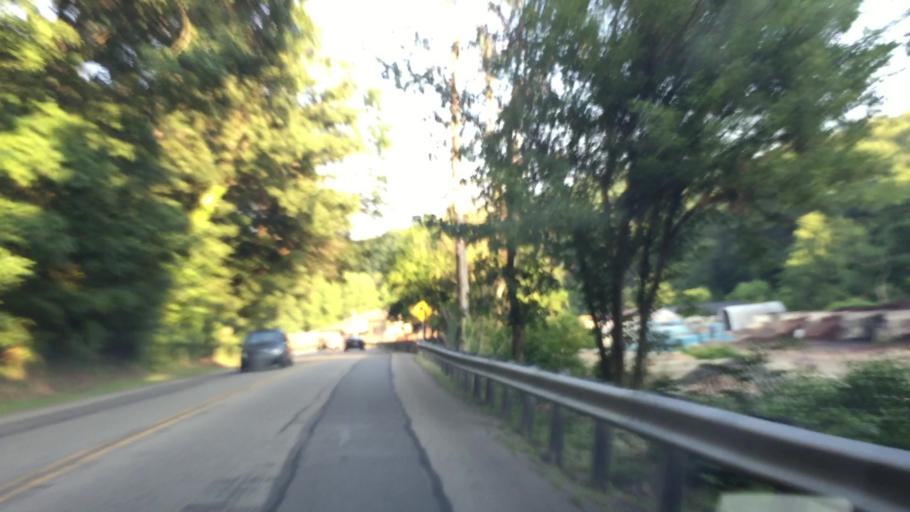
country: US
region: Pennsylvania
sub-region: Allegheny County
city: South Park Township
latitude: 40.2880
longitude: -80.0041
